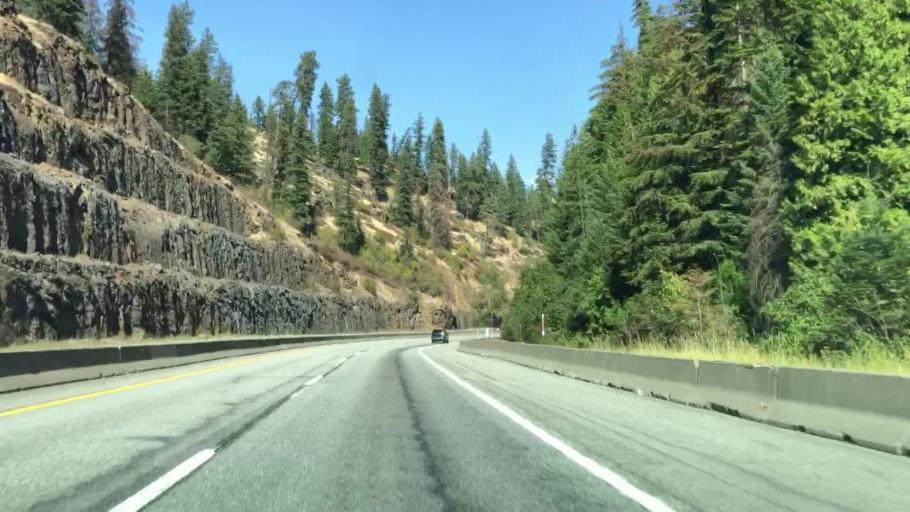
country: US
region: Idaho
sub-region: Kootenai County
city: Coeur d'Alene
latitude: 47.6234
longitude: -116.5734
